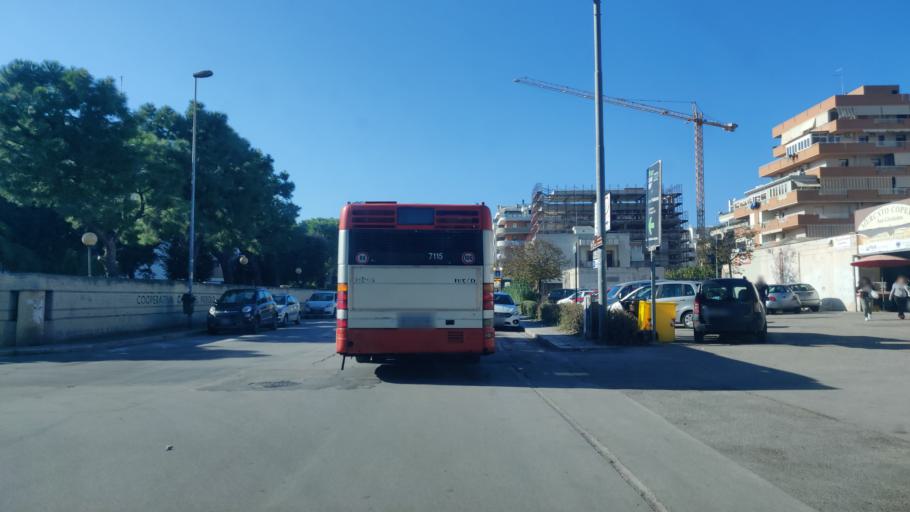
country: IT
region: Apulia
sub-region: Provincia di Bari
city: San Paolo
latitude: 41.1365
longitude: 16.8192
